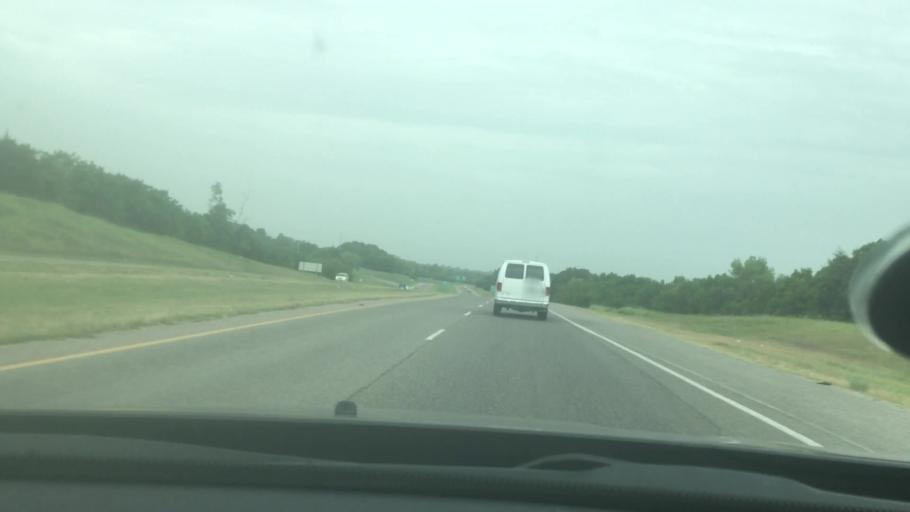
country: US
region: Oklahoma
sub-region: Pontotoc County
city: Ada
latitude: 34.7417
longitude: -96.6474
